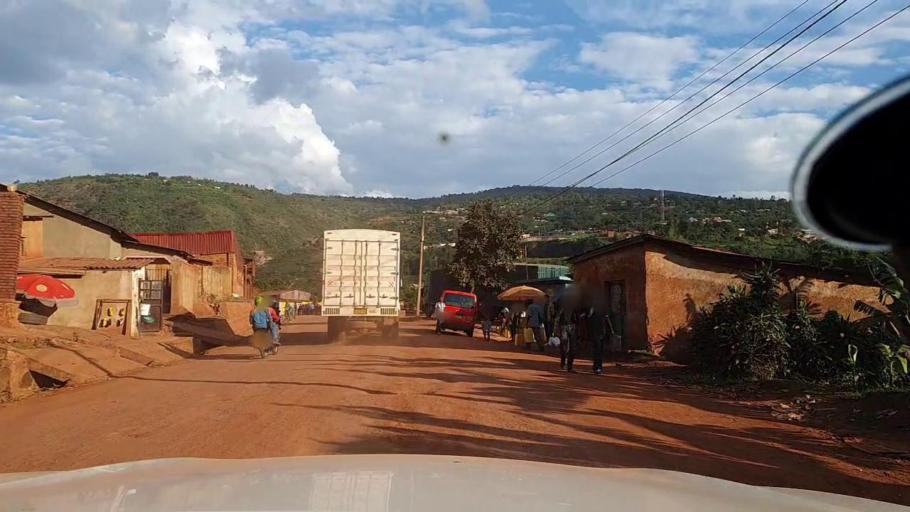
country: RW
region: Kigali
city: Kigali
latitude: -1.9478
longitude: 30.0191
